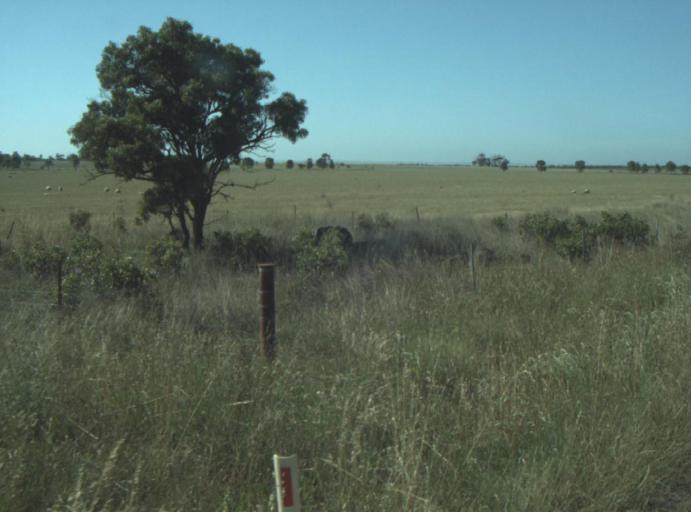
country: AU
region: Victoria
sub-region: Wyndham
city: Little River
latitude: -37.9647
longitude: 144.4627
